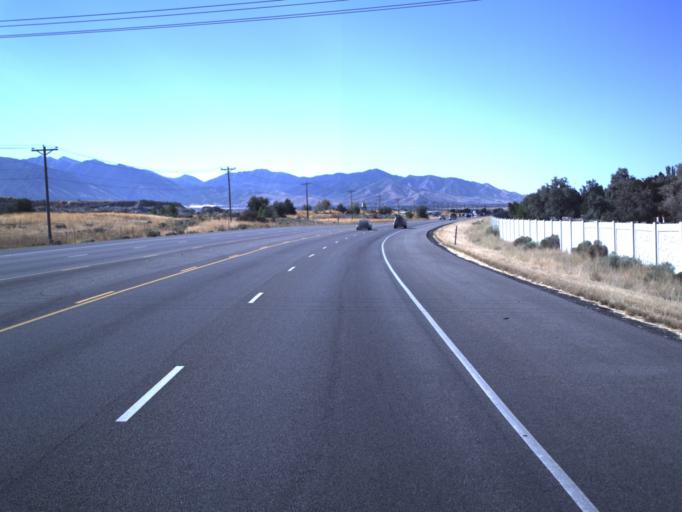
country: US
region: Utah
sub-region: Tooele County
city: Stansbury park
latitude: 40.6424
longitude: -112.2879
